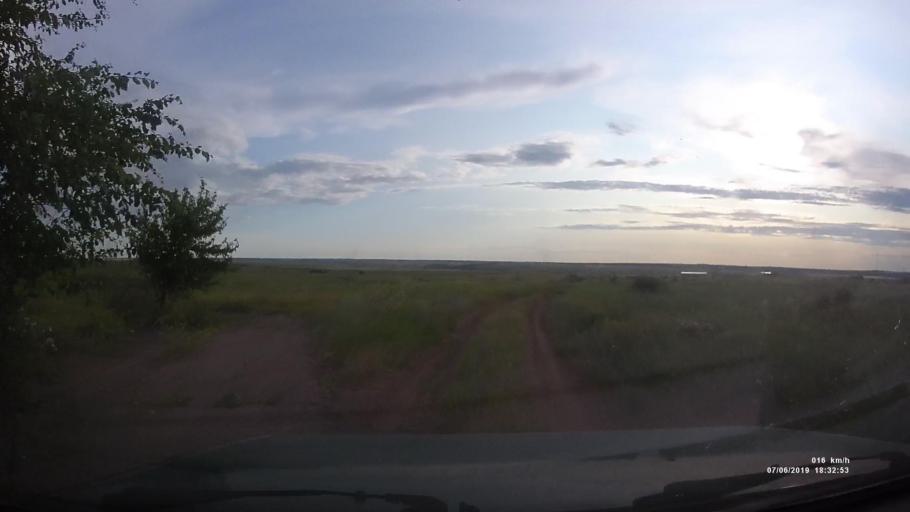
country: RU
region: Rostov
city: Staraya Stanitsa
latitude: 48.2624
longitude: 40.3642
